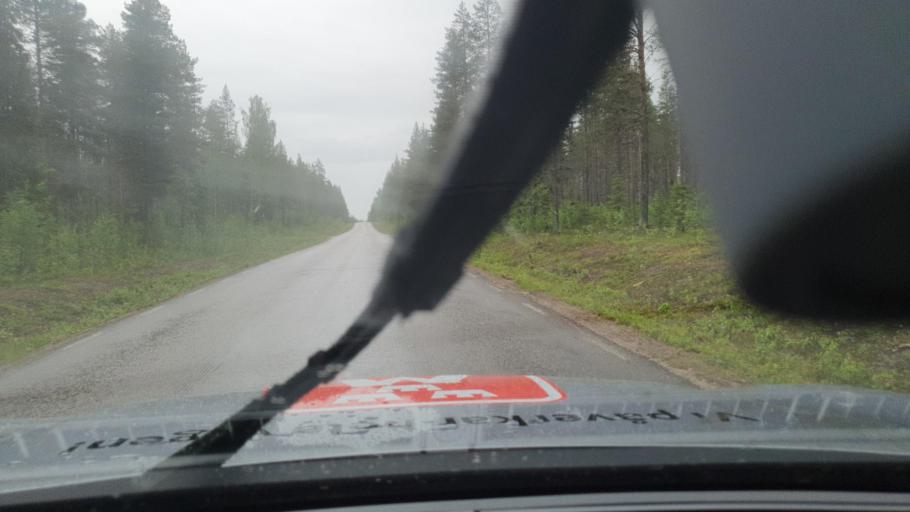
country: SE
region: Norrbotten
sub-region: Pajala Kommun
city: Pajala
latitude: 66.8328
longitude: 23.1087
